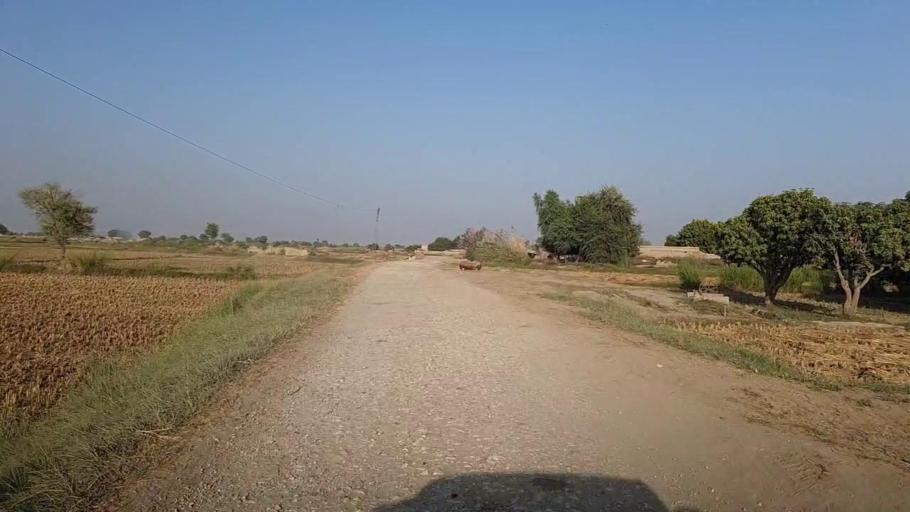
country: PK
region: Sindh
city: Kashmor
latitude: 28.4218
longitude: 69.4210
